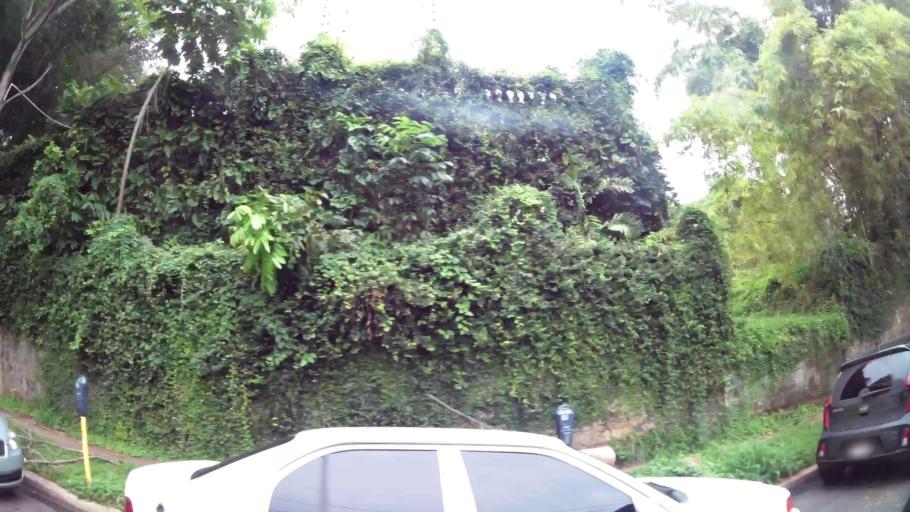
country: PA
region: Panama
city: Panama
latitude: 8.9777
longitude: -79.5298
